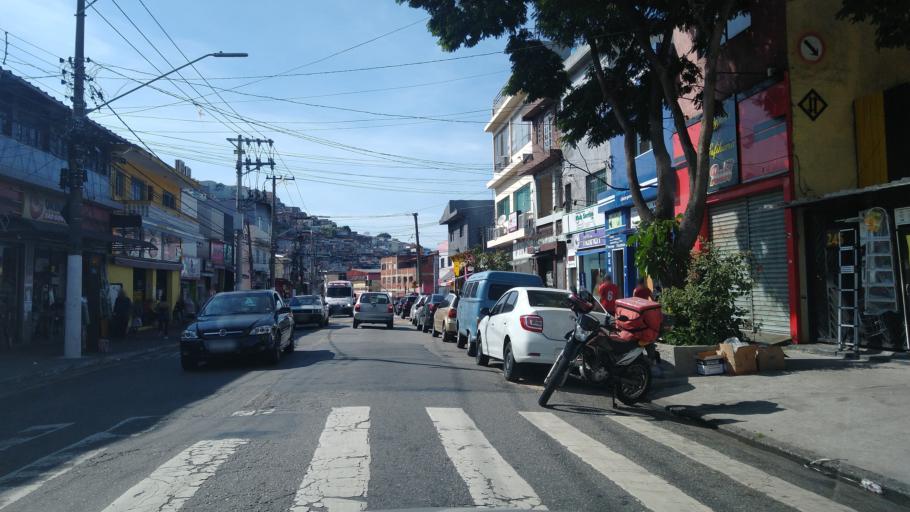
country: BR
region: Sao Paulo
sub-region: Sao Paulo
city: Sao Paulo
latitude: -23.4604
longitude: -46.6768
